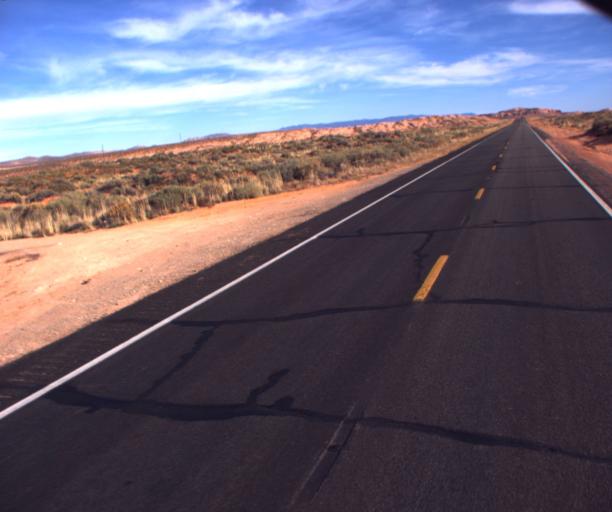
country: US
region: Arizona
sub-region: Apache County
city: Many Farms
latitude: 36.9375
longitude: -109.6367
